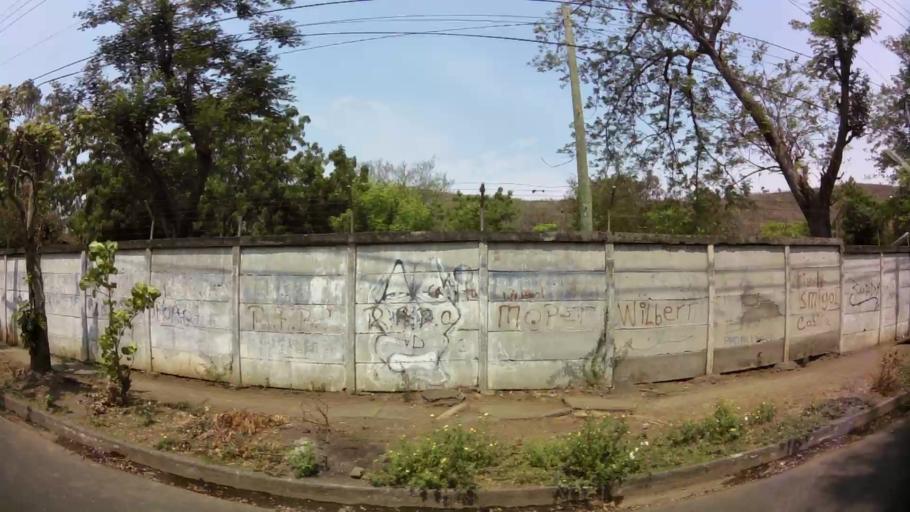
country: NI
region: Managua
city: Ciudad Sandino
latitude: 12.1553
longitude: -86.3148
